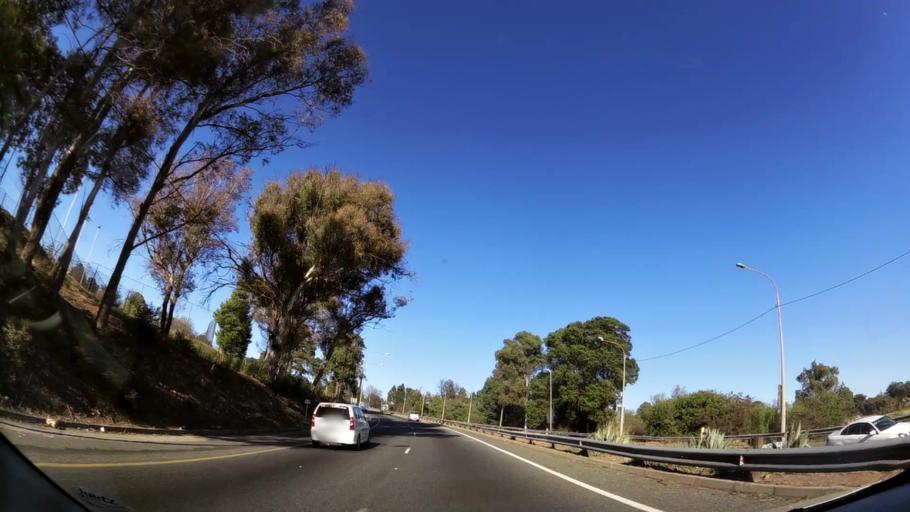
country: ZA
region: Gauteng
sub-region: West Rand District Municipality
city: Krugersdorp
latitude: -26.0792
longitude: 27.7906
